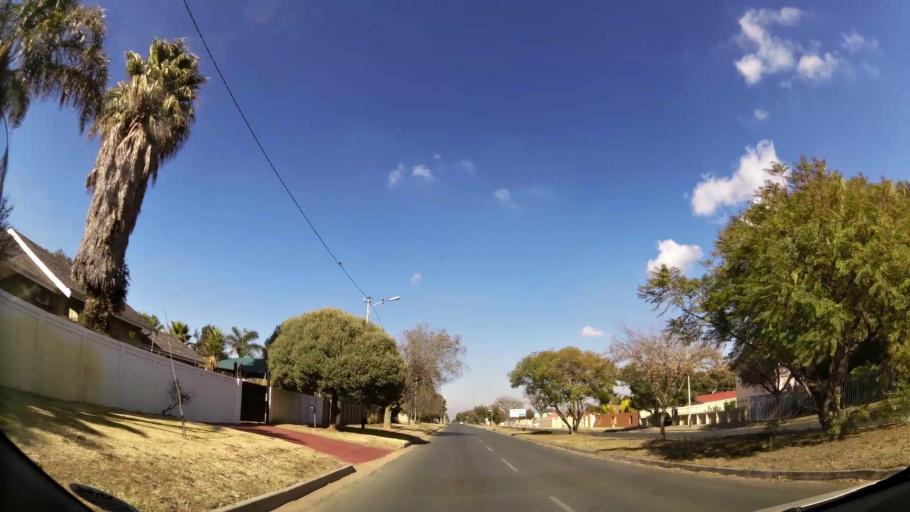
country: ZA
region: Gauteng
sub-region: City of Johannesburg Metropolitan Municipality
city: Roodepoort
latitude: -26.1432
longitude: 27.8263
